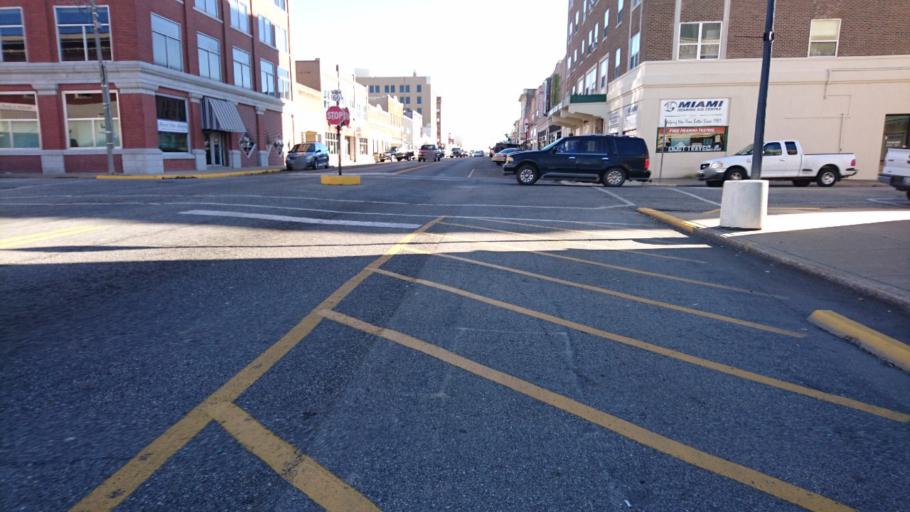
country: US
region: Oklahoma
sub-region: Ottawa County
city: Miami
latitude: 36.8764
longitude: -94.8776
